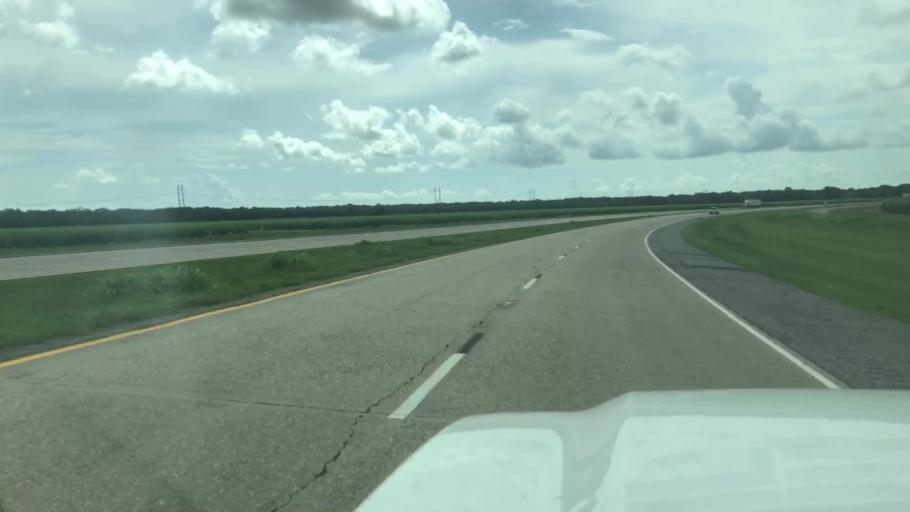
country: US
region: Louisiana
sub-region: Saint Mary Parish
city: Franklin
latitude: 29.7582
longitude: -91.4729
